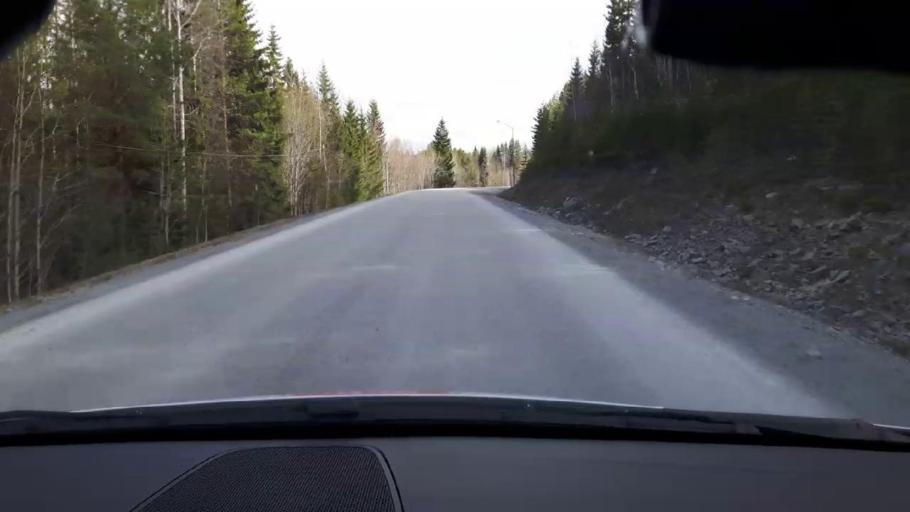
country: SE
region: Jaemtland
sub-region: Bergs Kommun
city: Hoverberg
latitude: 62.7297
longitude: 14.5980
